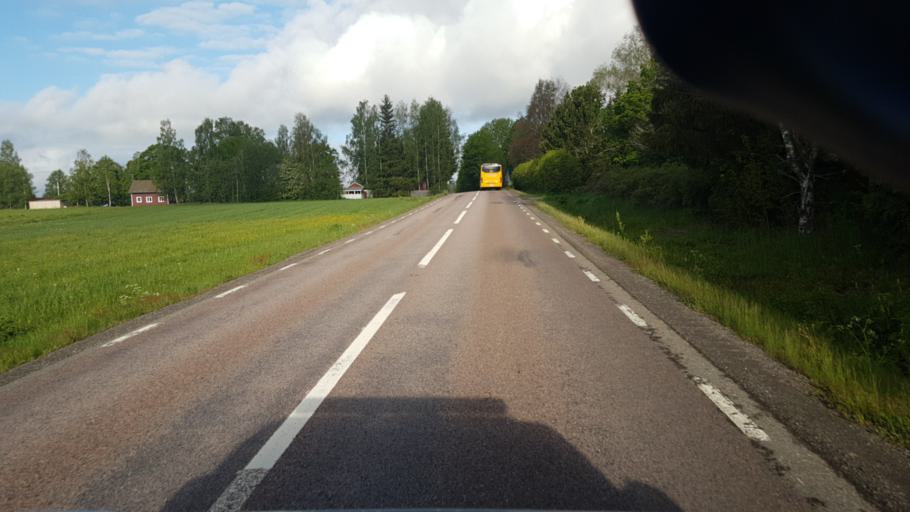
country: SE
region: Vaermland
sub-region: Eda Kommun
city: Amotfors
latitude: 59.7770
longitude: 12.2976
